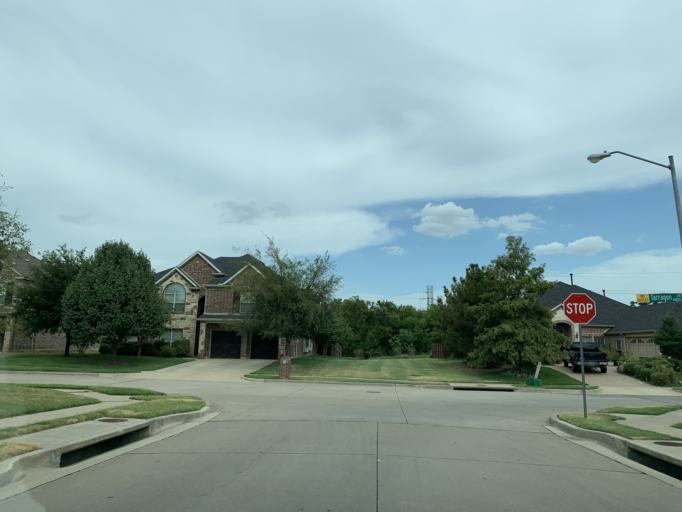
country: US
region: Texas
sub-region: Tarrant County
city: Arlington
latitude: 32.6554
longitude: -97.0459
